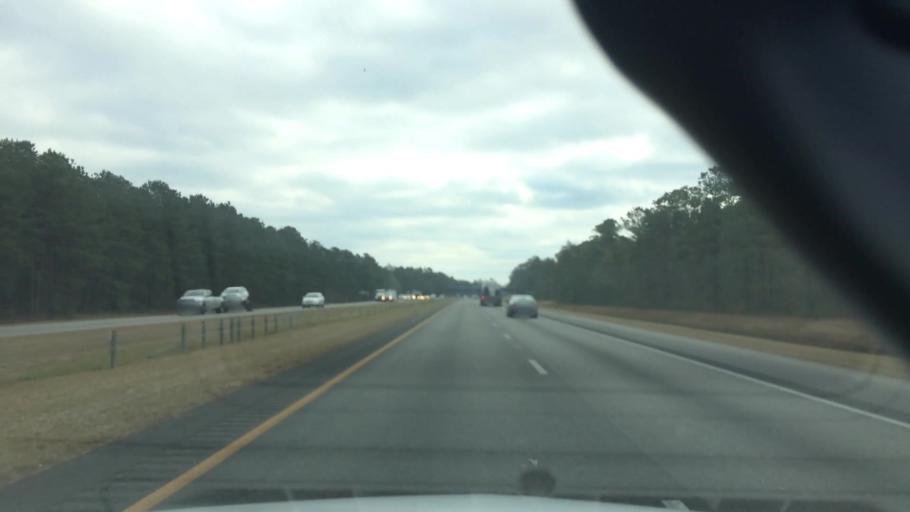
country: US
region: North Carolina
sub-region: New Hanover County
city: Skippers Corner
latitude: 34.3330
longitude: -77.8757
